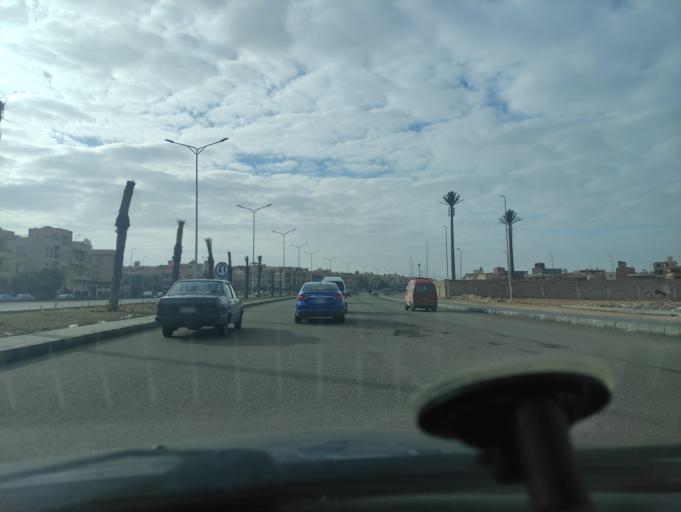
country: EG
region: Muhafazat al Qalyubiyah
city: Al Khankah
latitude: 30.0485
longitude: 31.4424
